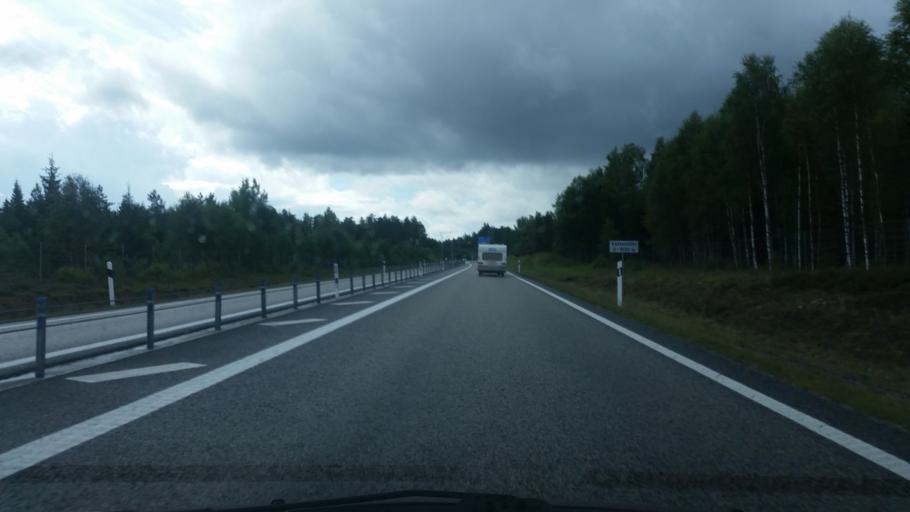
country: SE
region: Joenkoeping
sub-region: Gislaveds Kommun
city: Gislaved
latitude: 57.3442
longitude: 13.5532
